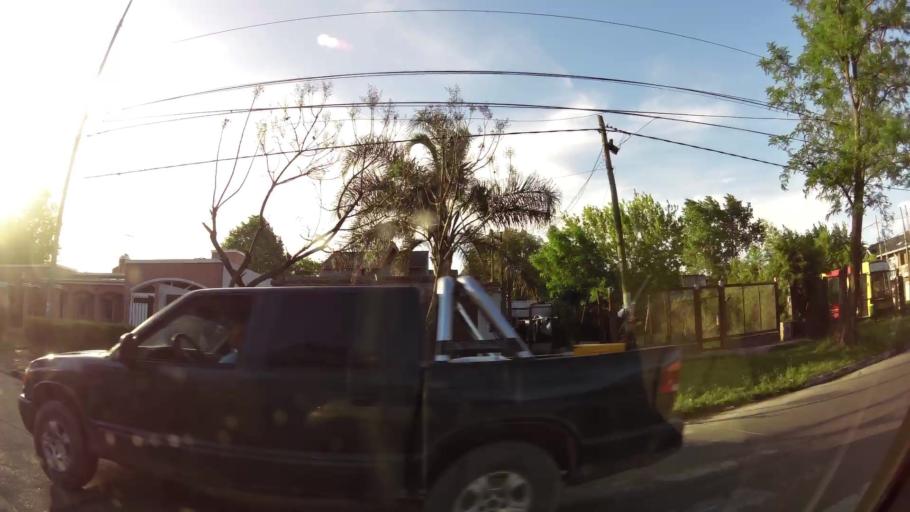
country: AR
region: Buenos Aires
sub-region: Partido de Quilmes
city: Quilmes
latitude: -34.7859
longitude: -58.2101
